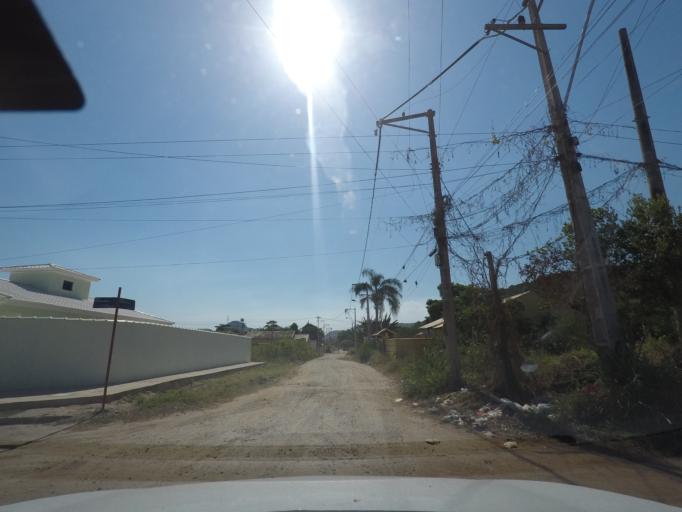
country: BR
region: Rio de Janeiro
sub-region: Niteroi
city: Niteroi
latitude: -22.9596
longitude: -42.9711
